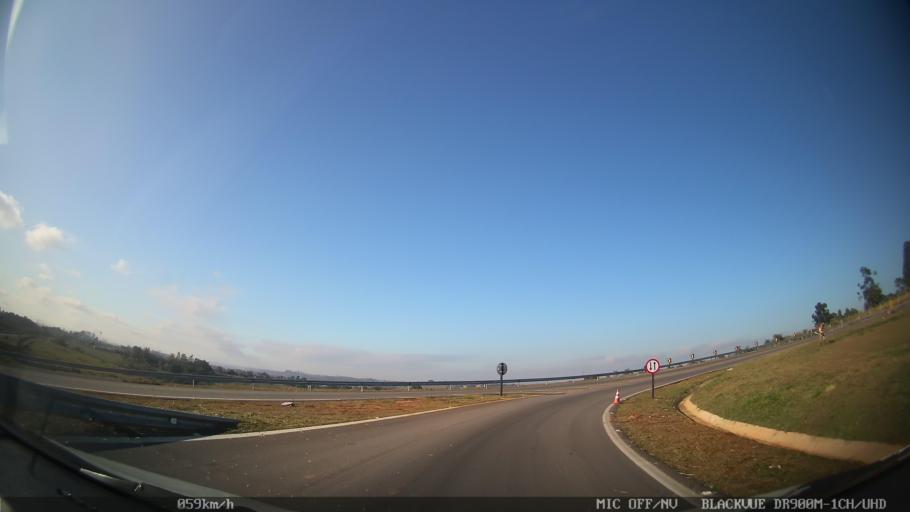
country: BR
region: Sao Paulo
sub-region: Hortolandia
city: Hortolandia
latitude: -22.8865
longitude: -47.1567
